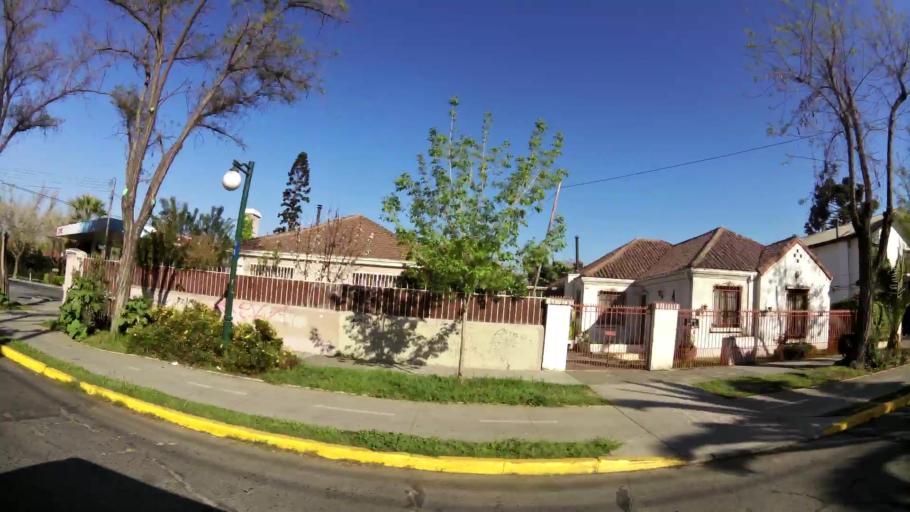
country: CL
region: Santiago Metropolitan
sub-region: Provincia de Santiago
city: Villa Presidente Frei, Nunoa, Santiago, Chile
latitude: -33.4508
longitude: -70.5853
